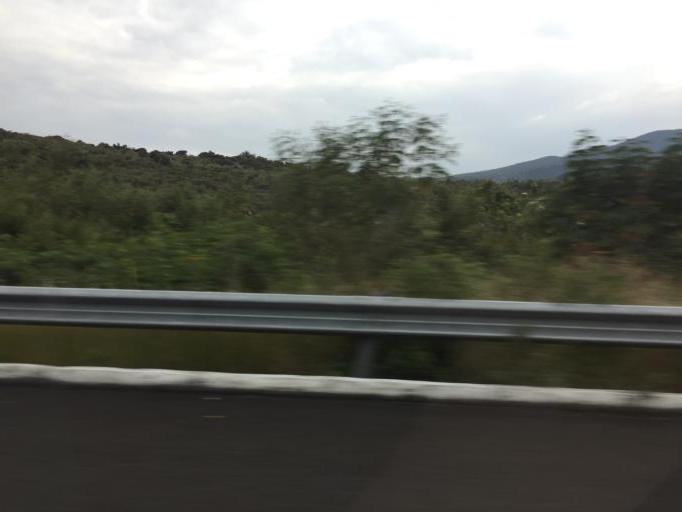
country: MX
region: Michoacan
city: Panindicuaro de la Reforma
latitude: 19.9667
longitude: -101.7033
